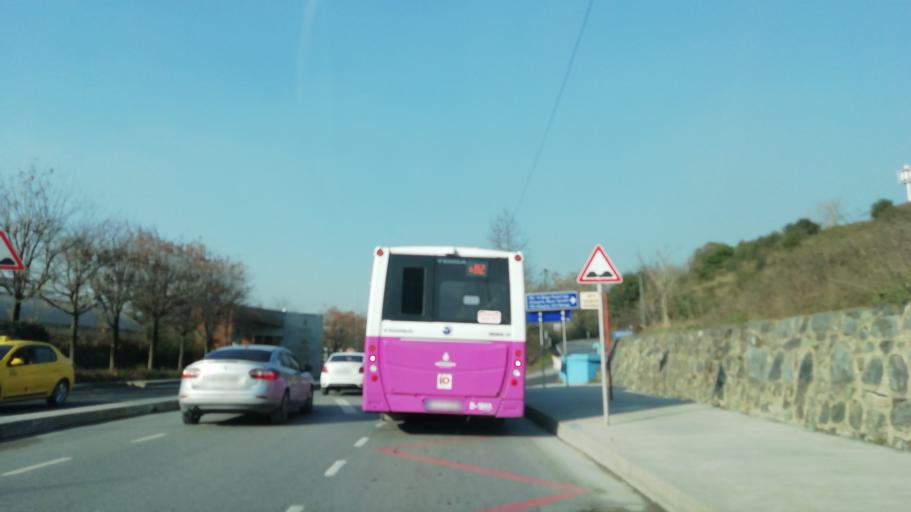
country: TR
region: Istanbul
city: Sultangazi
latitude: 41.0931
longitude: 28.9275
